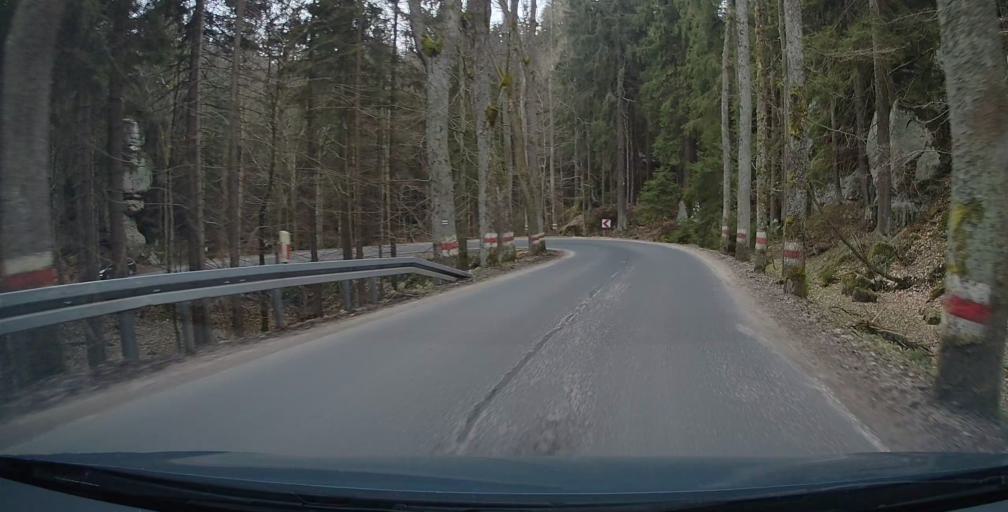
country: PL
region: Lower Silesian Voivodeship
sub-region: Powiat klodzki
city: Radkow
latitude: 50.4757
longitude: 16.3925
